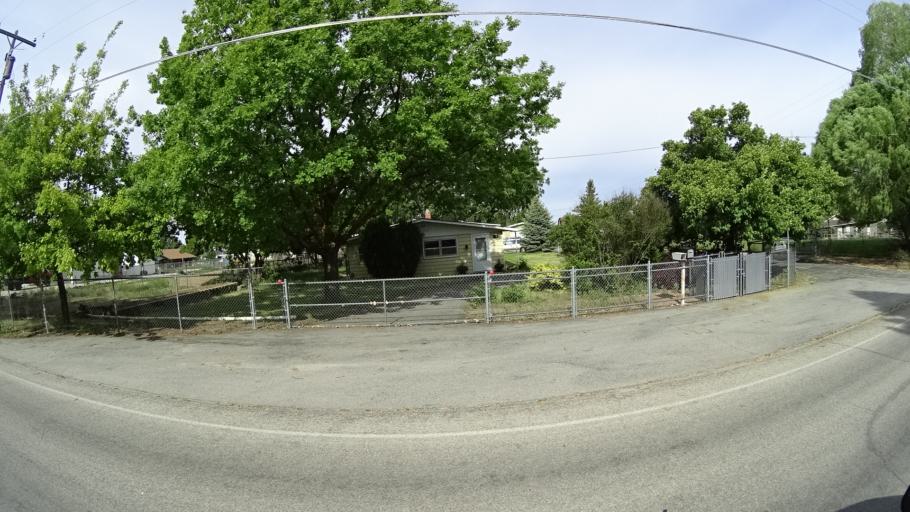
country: US
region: Idaho
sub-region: Ada County
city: Garden City
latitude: 43.5703
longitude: -116.3042
